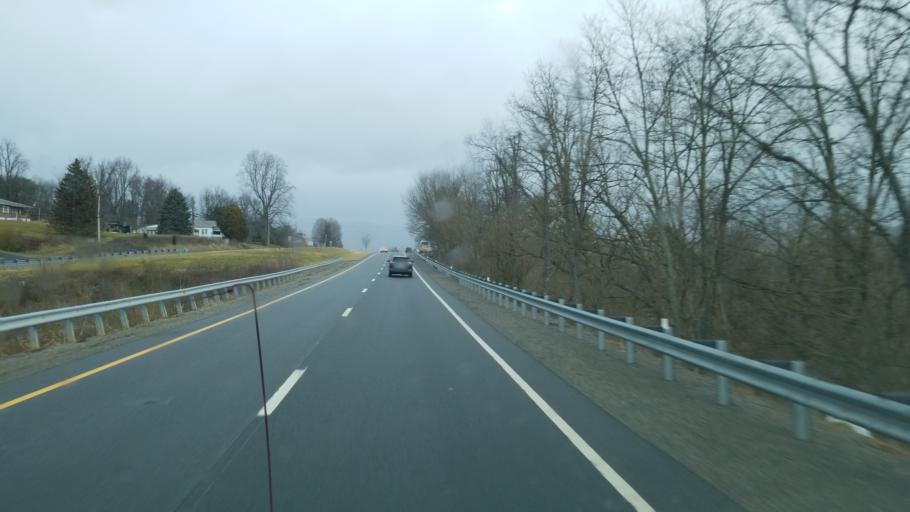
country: US
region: Virginia
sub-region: Giles County
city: Pearisburg
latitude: 37.3050
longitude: -80.7372
